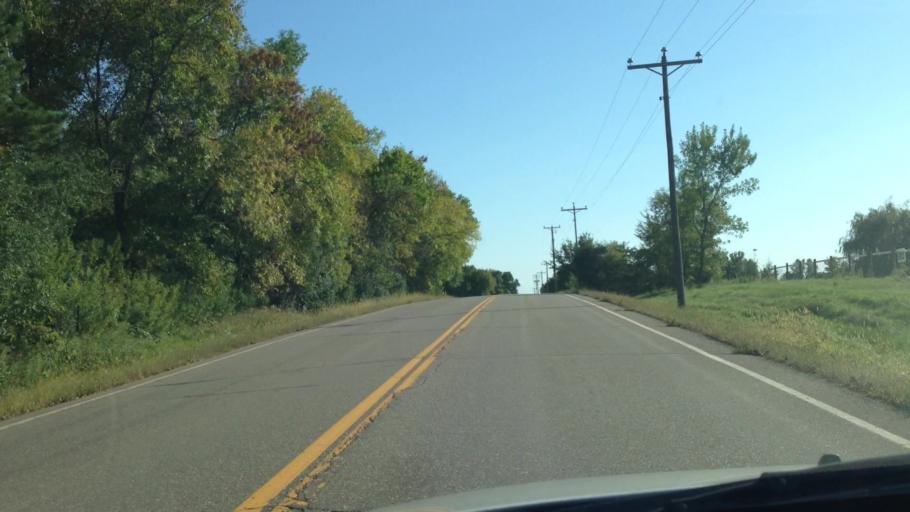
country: US
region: Minnesota
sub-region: Washington County
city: Stillwater
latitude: 45.0985
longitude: -92.8128
